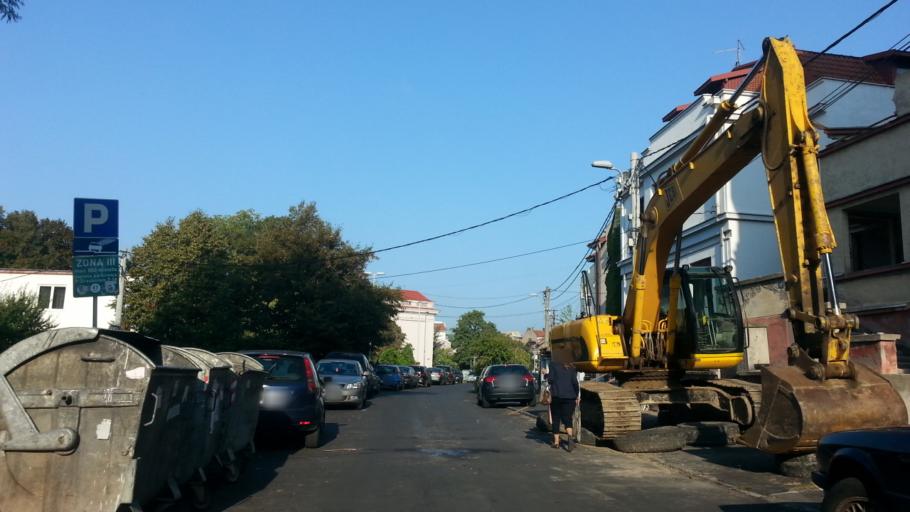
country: RS
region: Central Serbia
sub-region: Belgrade
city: Vracar
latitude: 44.7945
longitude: 20.4824
